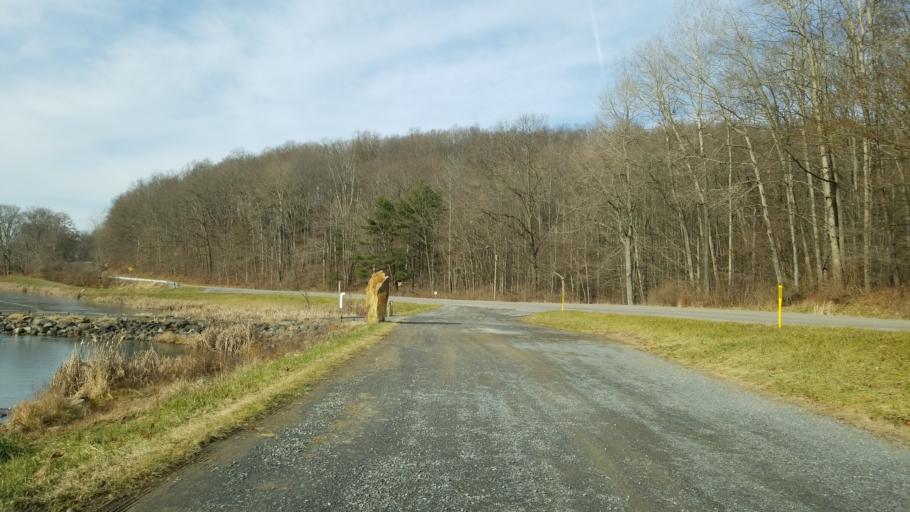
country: US
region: Pennsylvania
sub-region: Jefferson County
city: Albion
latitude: 40.9508
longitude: -78.9073
